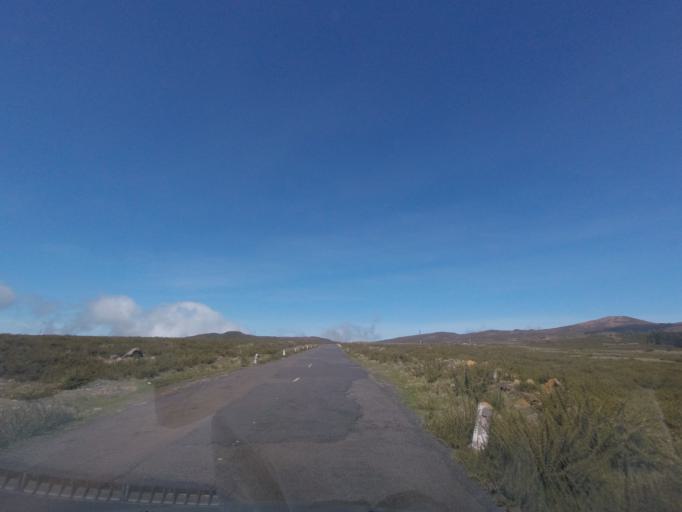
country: PT
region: Madeira
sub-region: Calheta
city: Arco da Calheta
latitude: 32.7516
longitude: -17.0987
